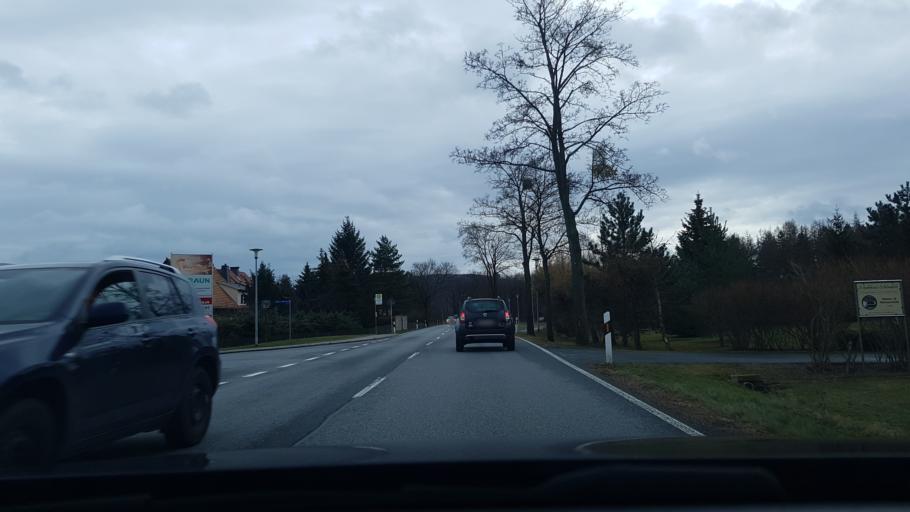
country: DE
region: Saxony
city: Dohma
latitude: 50.8830
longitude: 13.9552
